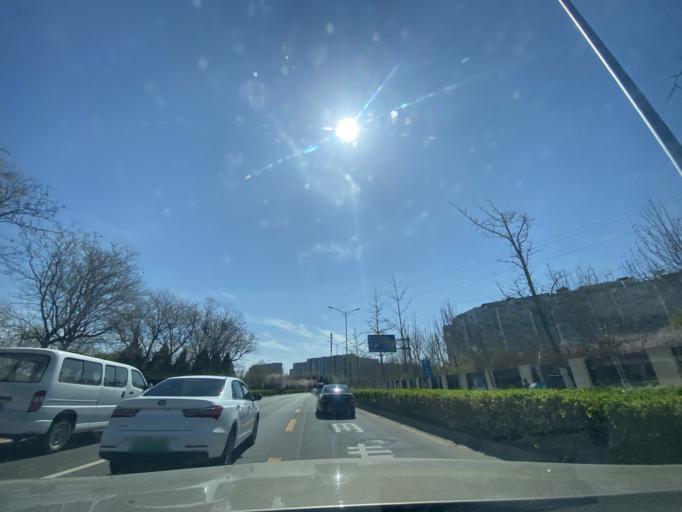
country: CN
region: Beijing
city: Sijiqing
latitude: 39.9339
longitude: 116.2456
